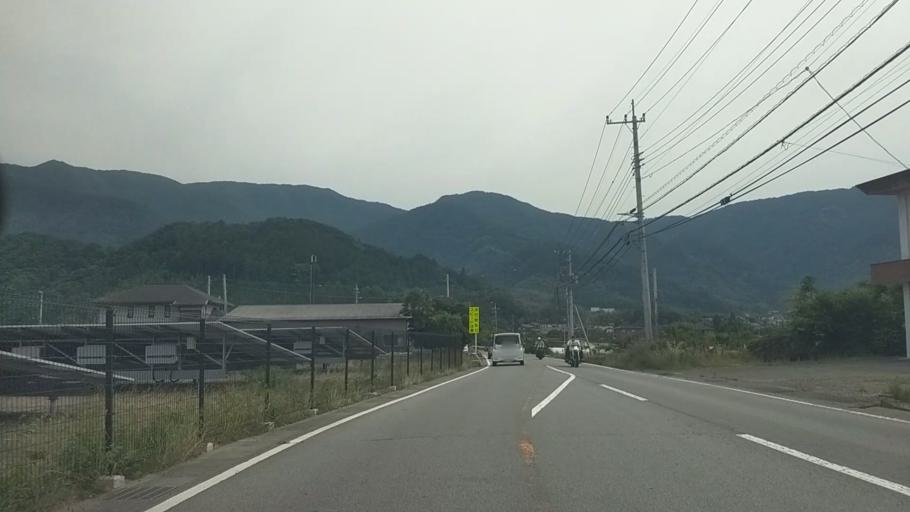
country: JP
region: Yamanashi
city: Isawa
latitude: 35.5814
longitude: 138.5919
